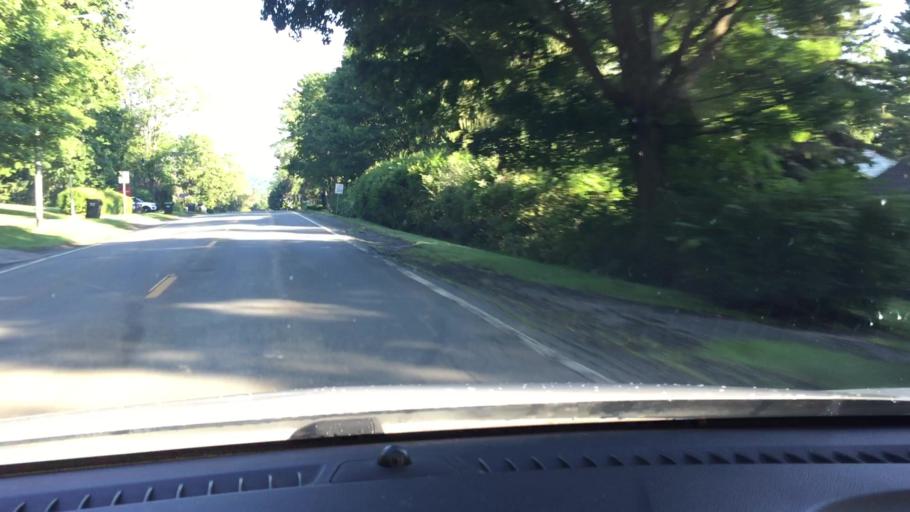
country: US
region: Massachusetts
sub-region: Berkshire County
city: Lenox
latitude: 42.3536
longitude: -73.2793
